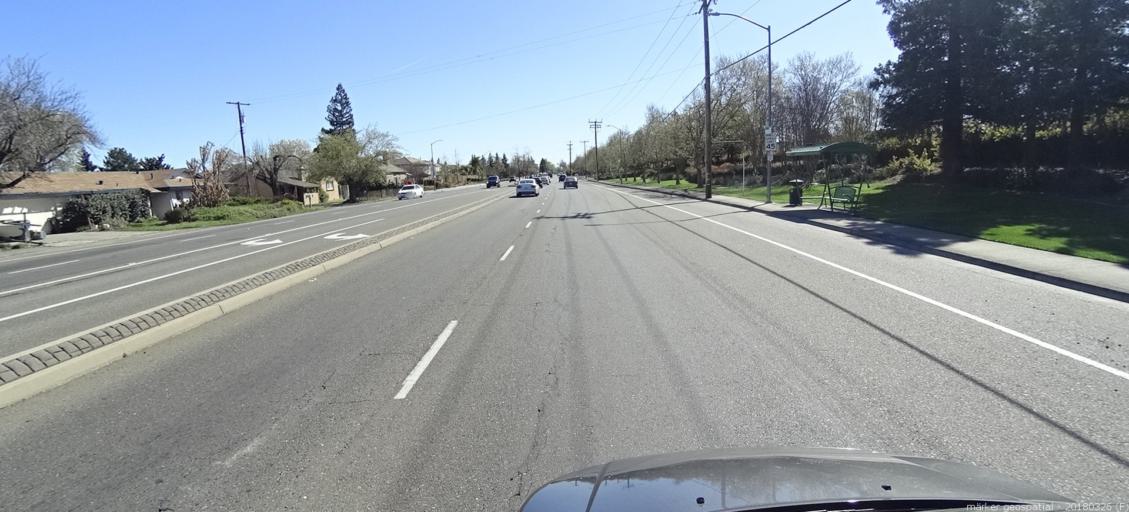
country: US
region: California
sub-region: Sacramento County
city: Vineyard
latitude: 38.4525
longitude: -121.3851
